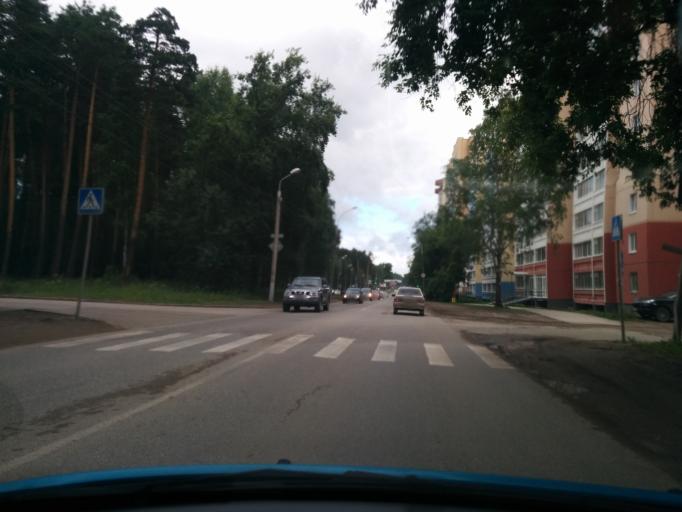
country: RU
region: Perm
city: Kondratovo
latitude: 58.0314
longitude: 56.0191
